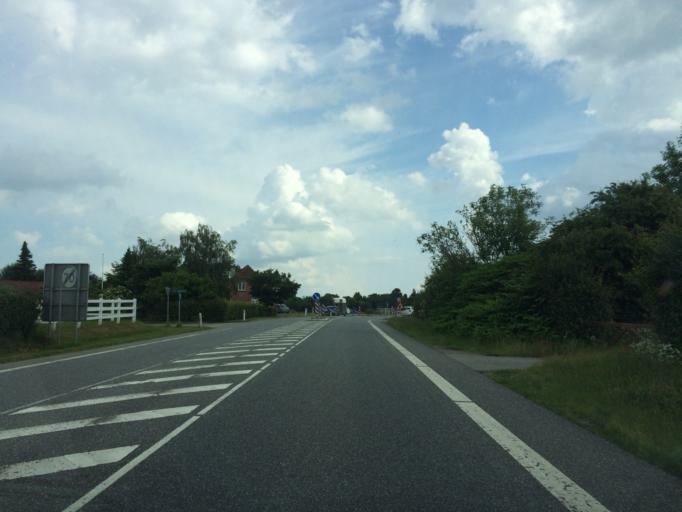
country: DK
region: South Denmark
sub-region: Fredericia Kommune
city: Snoghoj
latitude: 55.5359
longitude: 9.6910
